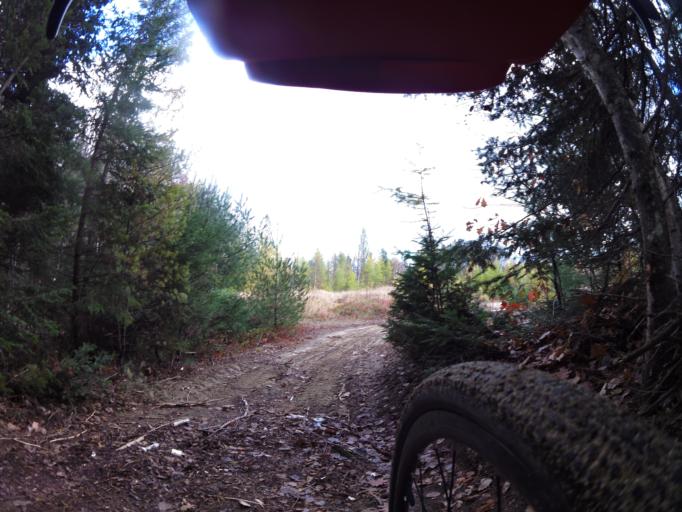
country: CA
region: Quebec
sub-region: Outaouais
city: Wakefield
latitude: 45.6713
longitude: -76.1282
